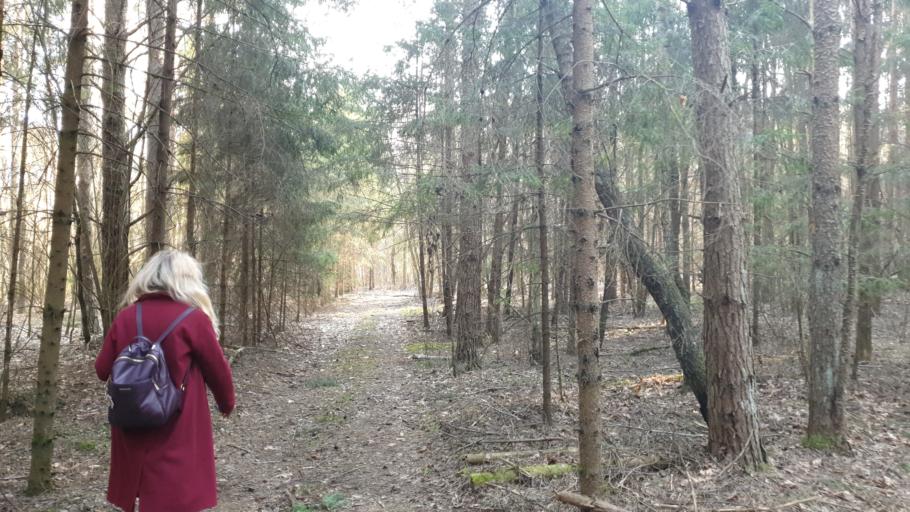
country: LT
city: Nemencine
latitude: 54.8758
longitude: 25.5737
